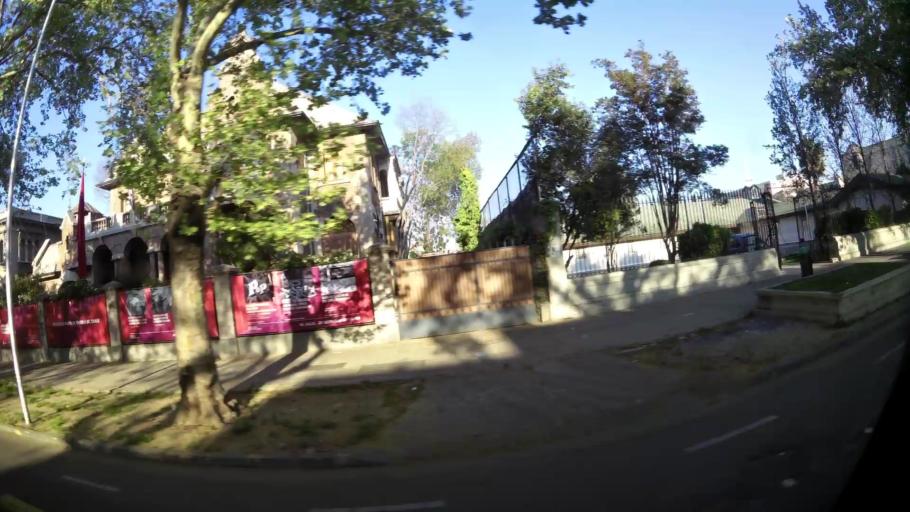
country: CL
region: Santiago Metropolitan
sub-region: Provincia de Santiago
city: Santiago
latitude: -33.4540
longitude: -70.6672
